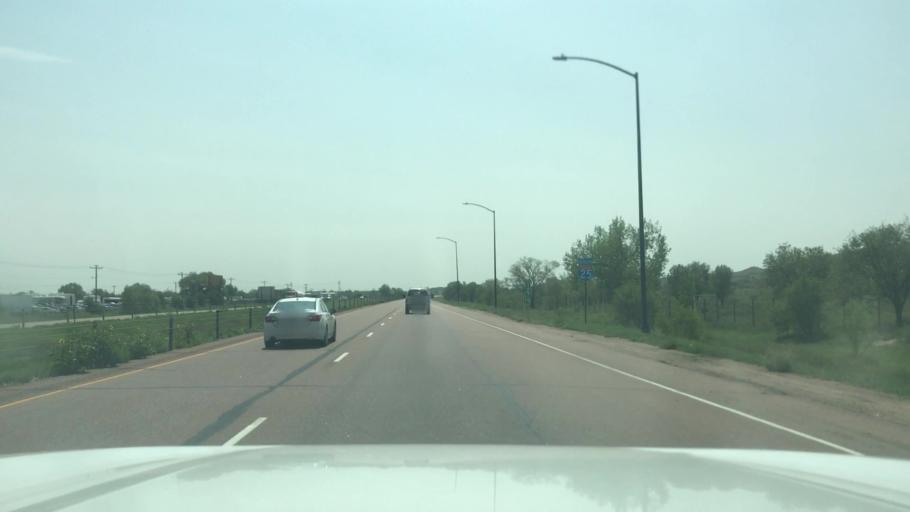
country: US
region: Colorado
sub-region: El Paso County
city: Fountain
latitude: 38.6685
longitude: -104.7057
